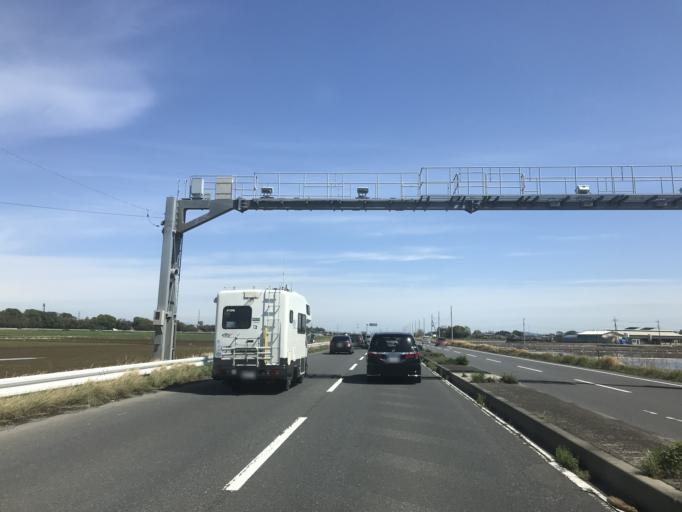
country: JP
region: Ibaraki
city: Ishige
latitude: 36.2074
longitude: 139.9847
